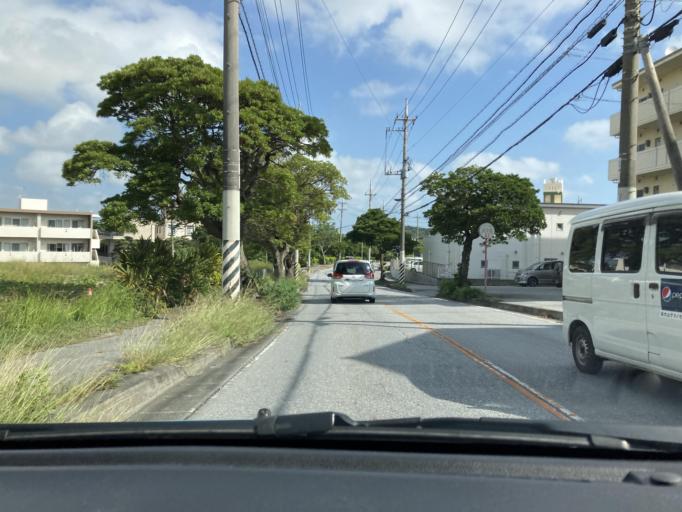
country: JP
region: Okinawa
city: Ginowan
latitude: 26.2551
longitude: 127.7747
